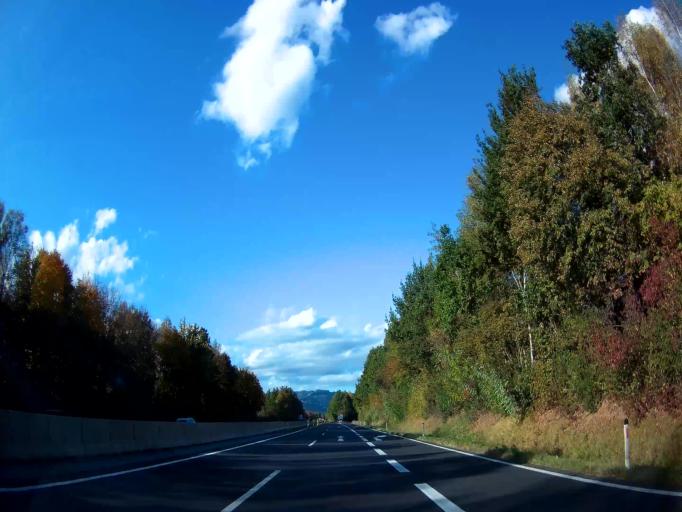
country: AT
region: Carinthia
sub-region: Politischer Bezirk Wolfsberg
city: Wolfsberg
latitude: 46.8193
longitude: 14.8221
